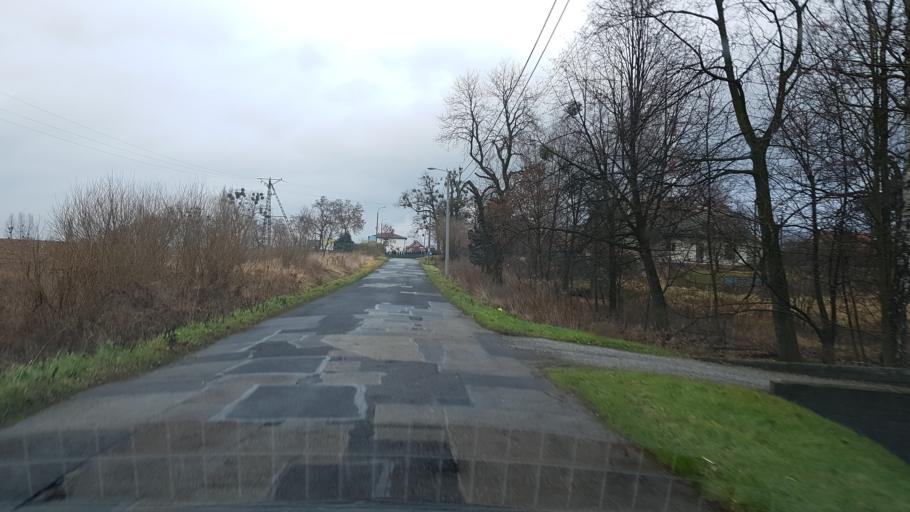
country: PL
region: Silesian Voivodeship
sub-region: Powiat pszczynski
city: Pszczyna
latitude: 49.9661
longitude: 18.9178
